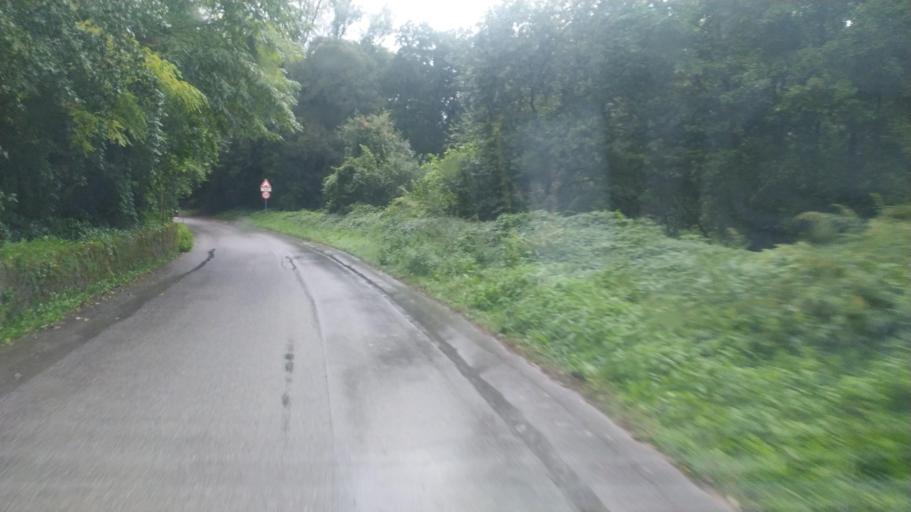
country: IT
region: Lombardy
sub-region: Provincia di Varese
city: Angera
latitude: 45.7679
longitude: 8.5922
